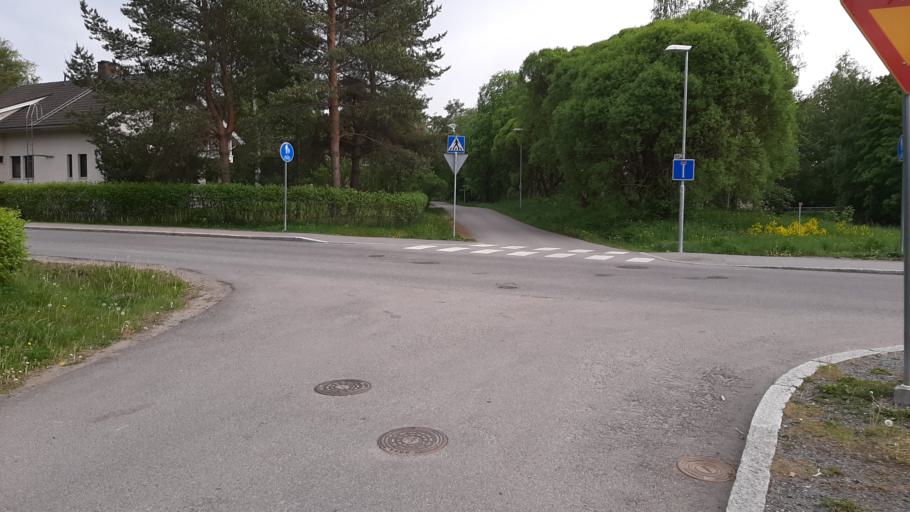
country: FI
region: Pirkanmaa
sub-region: Tampere
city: Tampere
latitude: 61.4745
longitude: 23.8474
